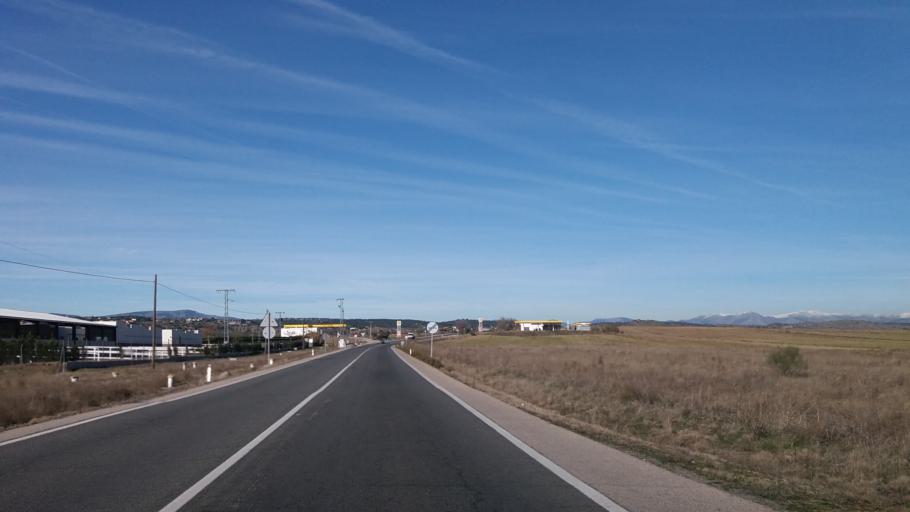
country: ES
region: Madrid
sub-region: Provincia de Madrid
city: Villanueva de la Canada
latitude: 40.4653
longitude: -4.0137
